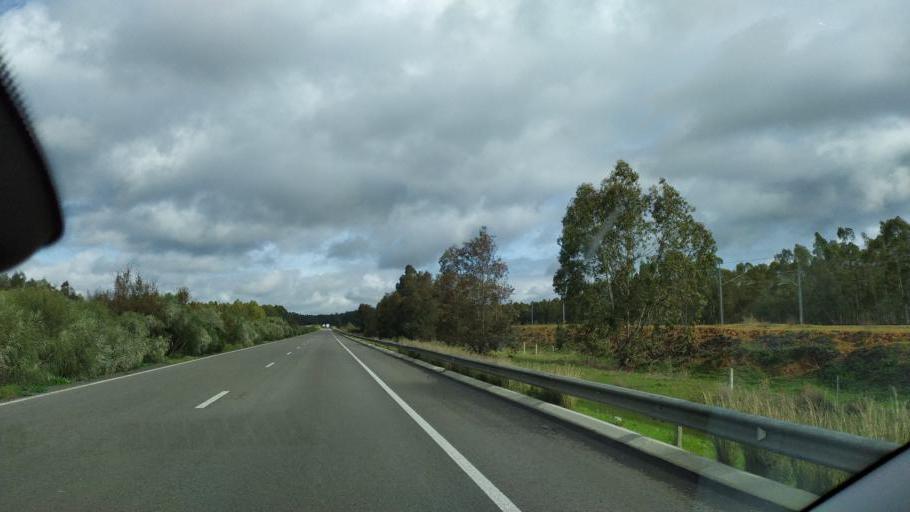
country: MA
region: Gharb-Chrarda-Beni Hssen
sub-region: Kenitra Province
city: Lalla Mimouna
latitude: 34.9099
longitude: -6.2064
